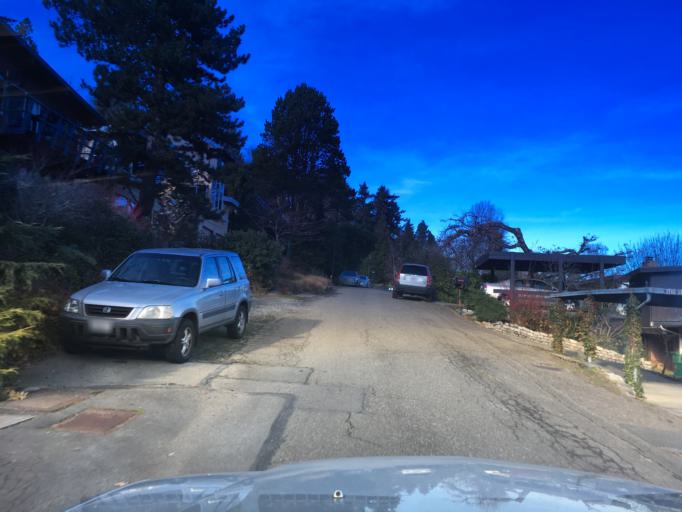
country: US
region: Washington
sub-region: King County
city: Inglewood-Finn Hill
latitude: 47.6851
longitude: -122.2671
